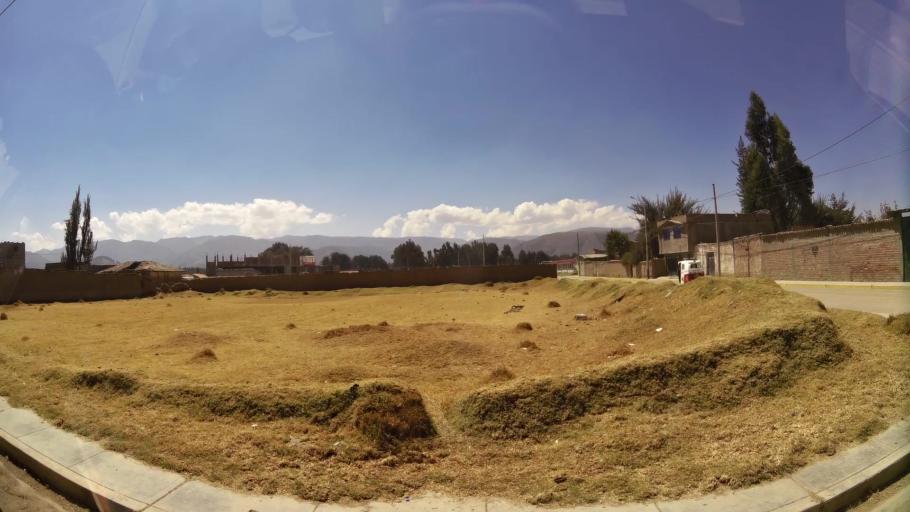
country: PE
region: Junin
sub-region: Provincia de Jauja
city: Jauja
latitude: -11.7729
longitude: -75.4932
